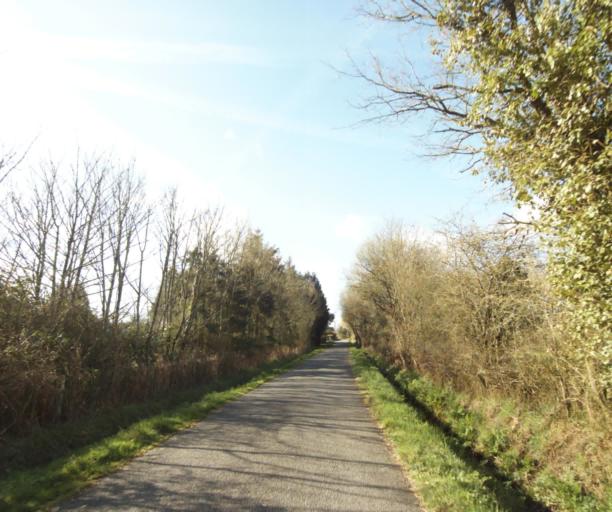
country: FR
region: Pays de la Loire
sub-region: Departement de la Loire-Atlantique
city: Bouvron
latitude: 47.4059
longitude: -1.8483
